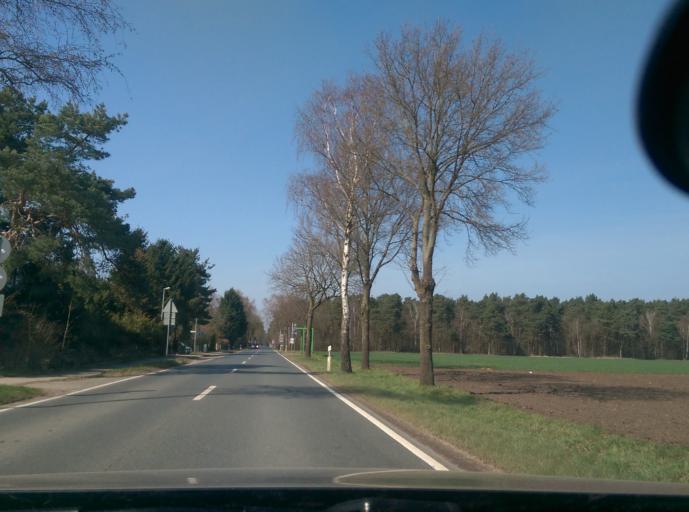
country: DE
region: Lower Saxony
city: Lindwedel
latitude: 52.5716
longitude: 9.6072
